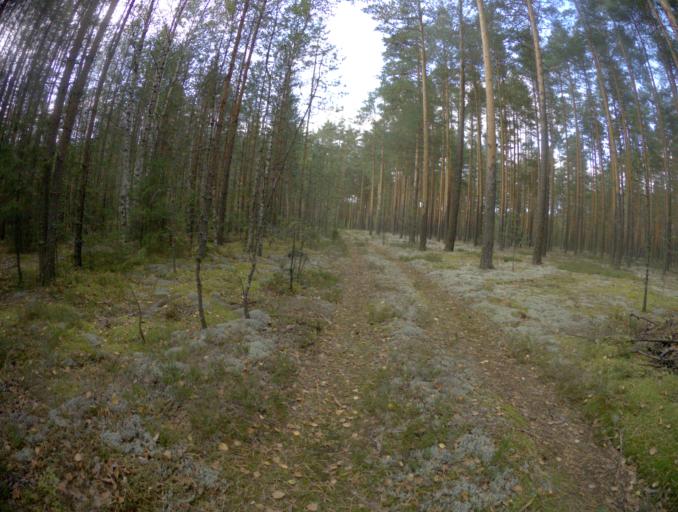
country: RU
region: Vladimir
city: Golovino
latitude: 55.8677
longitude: 40.3954
